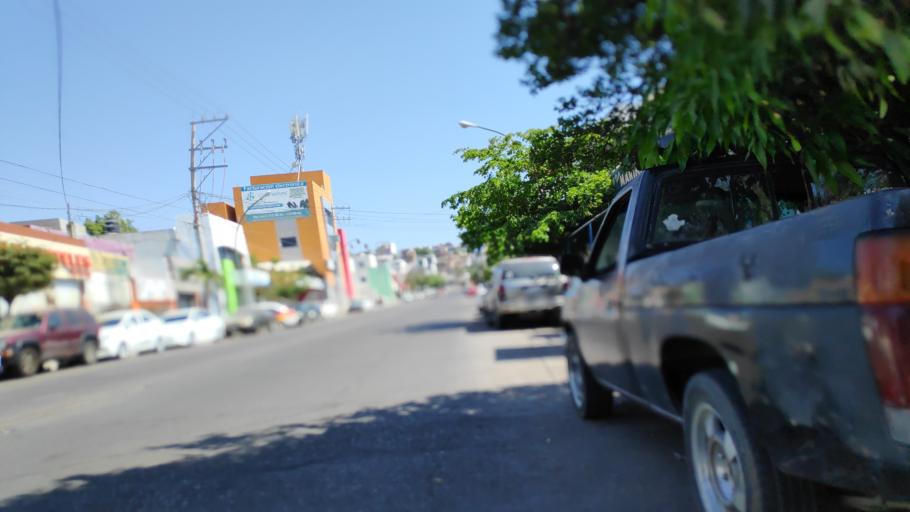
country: MX
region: Sinaloa
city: Culiacan
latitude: 24.7883
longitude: -107.4005
